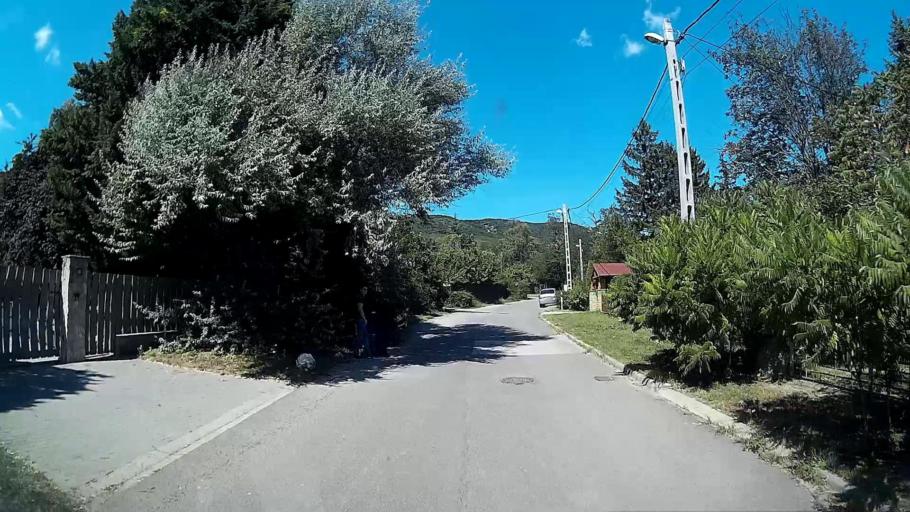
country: HU
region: Pest
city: Leanyfalu
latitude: 47.6974
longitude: 19.0787
